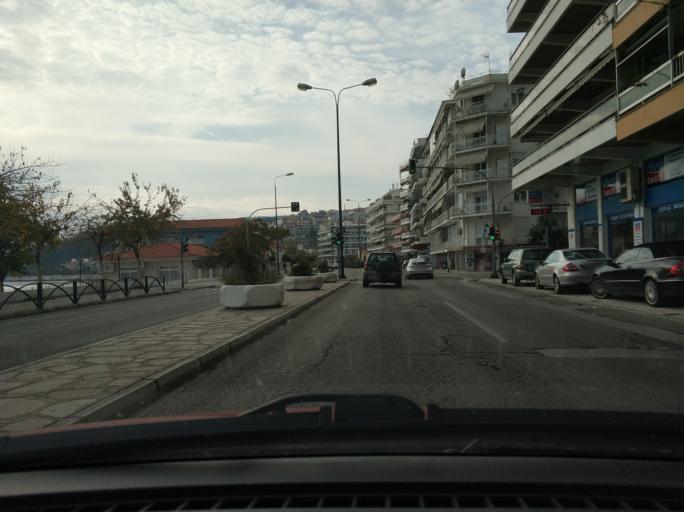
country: GR
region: East Macedonia and Thrace
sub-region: Nomos Kavalas
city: Kavala
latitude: 40.9351
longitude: 24.3969
